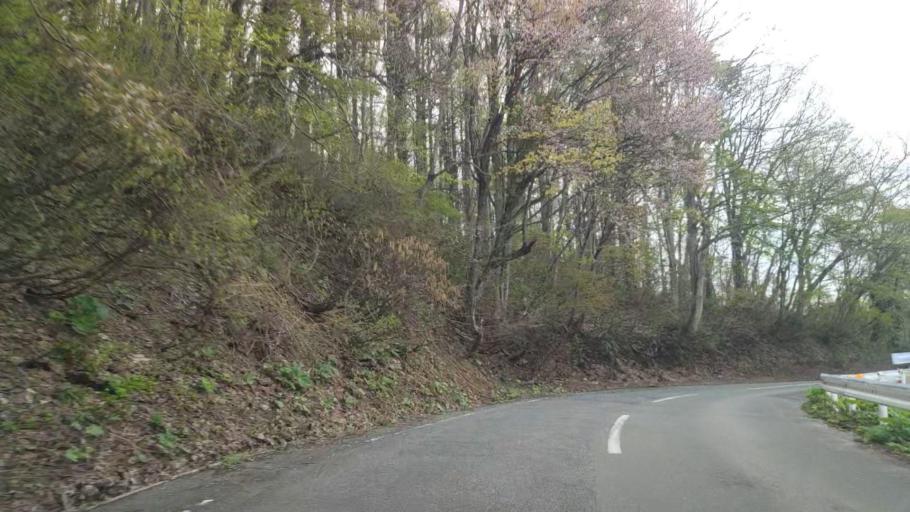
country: JP
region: Aomori
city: Aomori Shi
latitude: 40.7330
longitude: 140.8406
